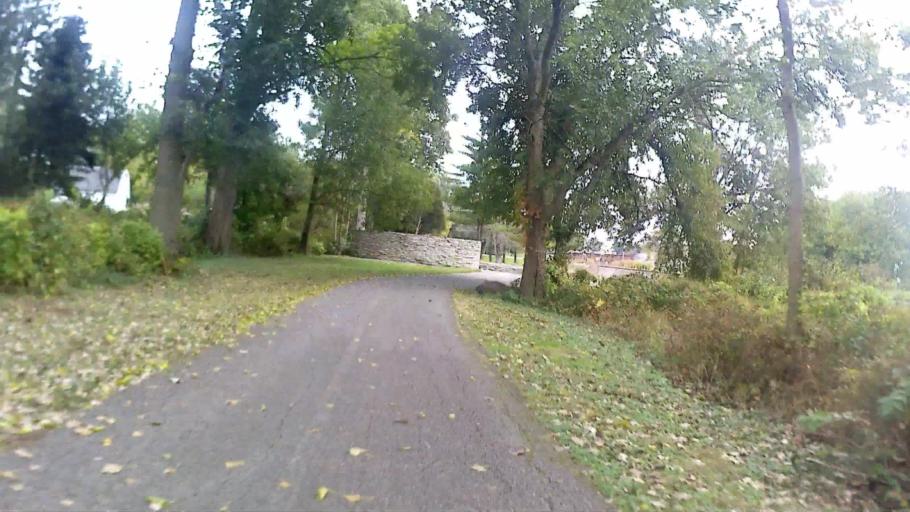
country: US
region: Illinois
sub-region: Kane County
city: Montgomery
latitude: 41.7467
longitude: -88.3604
